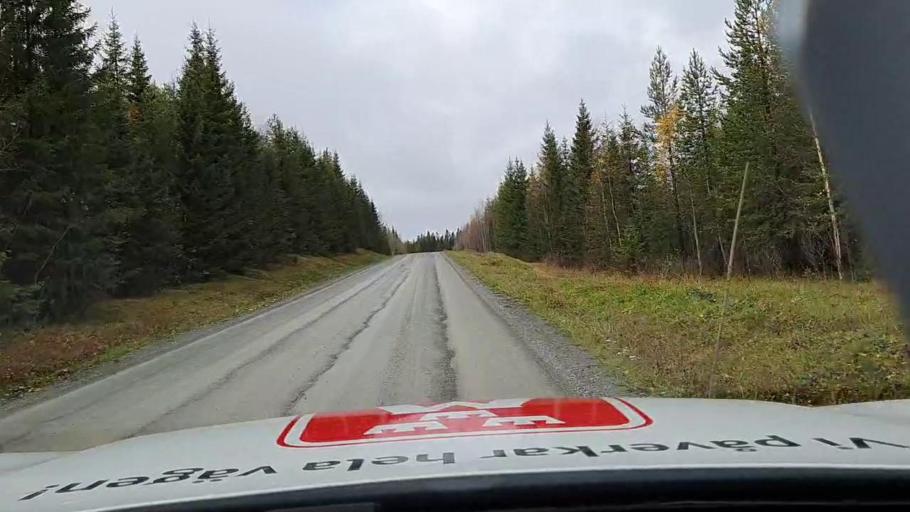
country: SE
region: Jaemtland
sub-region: Bergs Kommun
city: Hoverberg
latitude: 62.9994
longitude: 14.1460
